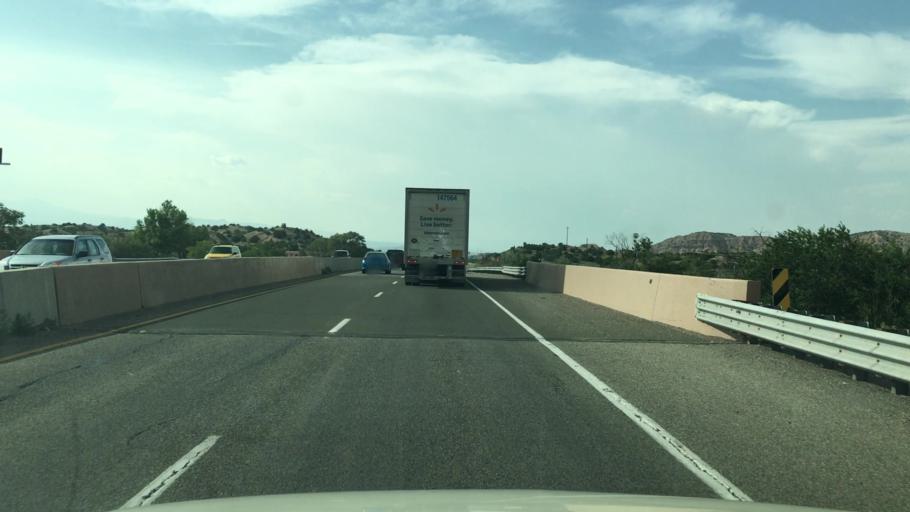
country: US
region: New Mexico
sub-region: Santa Fe County
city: Nambe
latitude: 35.8079
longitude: -105.9652
